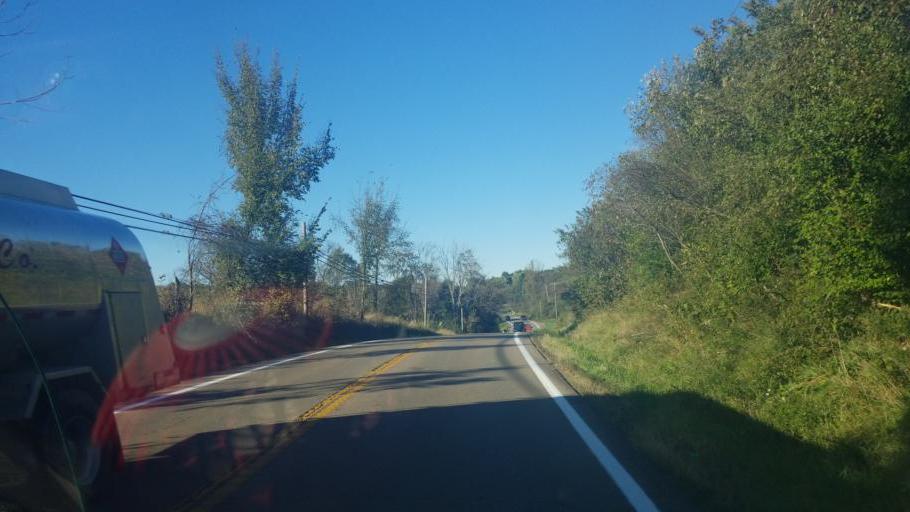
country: US
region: Ohio
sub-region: Columbiana County
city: New Waterford
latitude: 40.8071
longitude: -80.6364
